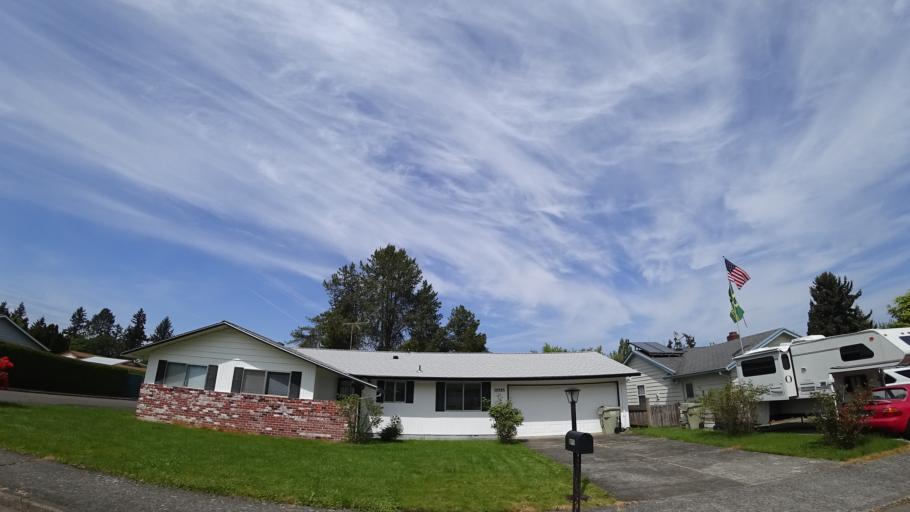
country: US
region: Oregon
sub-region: Washington County
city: Aloha
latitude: 45.4797
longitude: -122.8837
